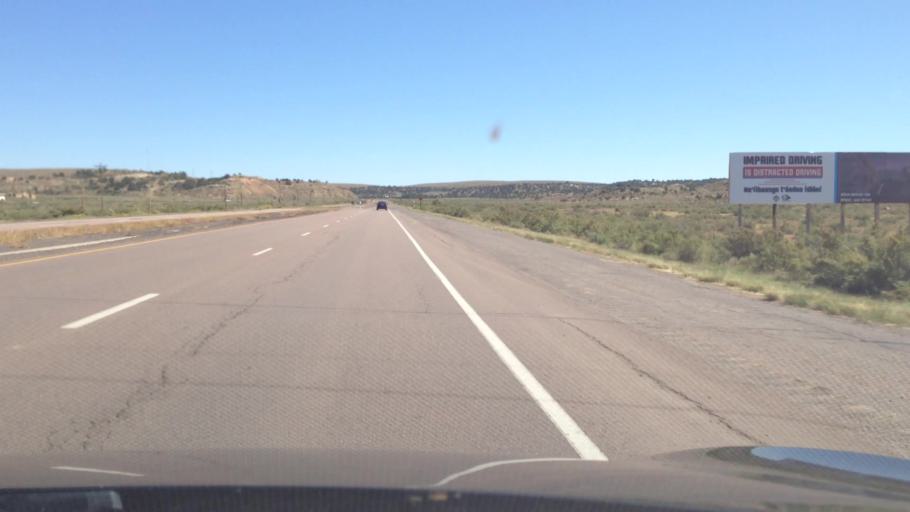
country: US
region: Arizona
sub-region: Apache County
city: Window Rock
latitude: 35.6479
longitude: -109.0337
